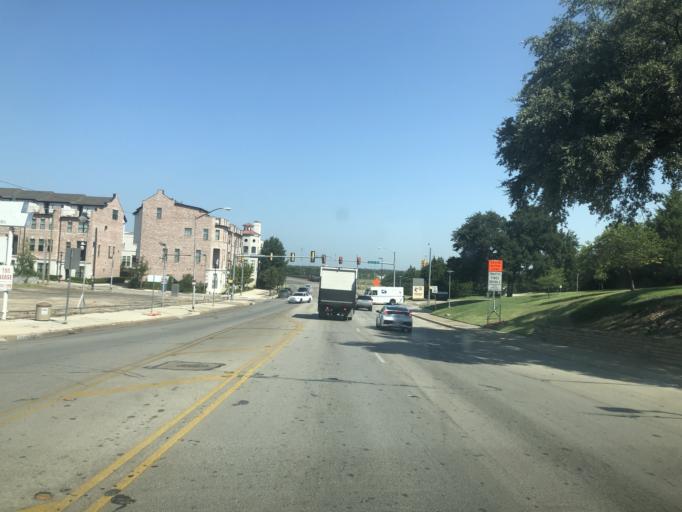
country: US
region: Texas
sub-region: Tarrant County
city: Fort Worth
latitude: 32.7555
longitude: -97.3397
